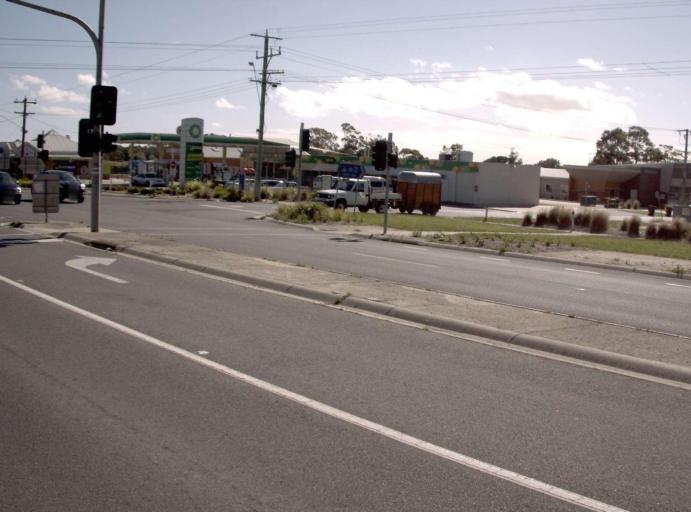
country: AU
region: Victoria
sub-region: Bass Coast
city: North Wonthaggi
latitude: -38.4072
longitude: 145.5306
